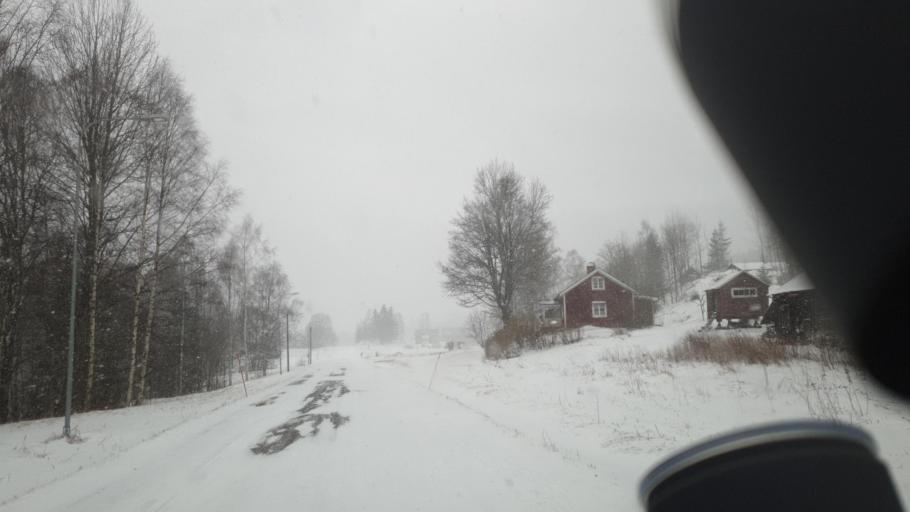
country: SE
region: Vaermland
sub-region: Arvika Kommun
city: Arvika
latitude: 59.7718
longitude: 12.7871
